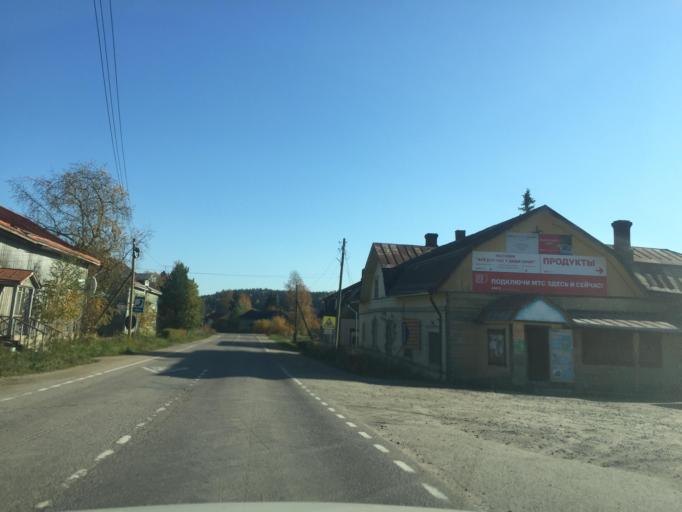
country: RU
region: Leningrad
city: Kuznechnoye
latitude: 61.2988
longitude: 29.8918
